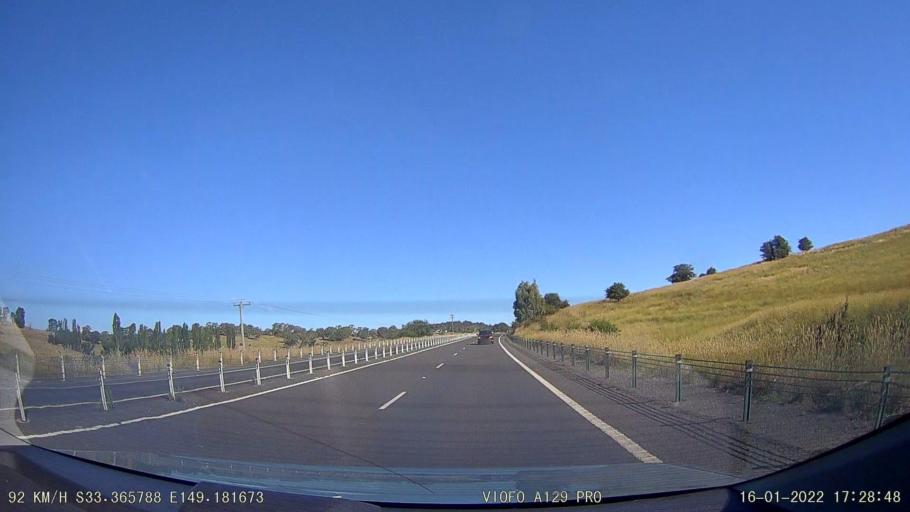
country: AU
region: New South Wales
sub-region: Blayney
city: Millthorpe
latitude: -33.3660
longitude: 149.1819
